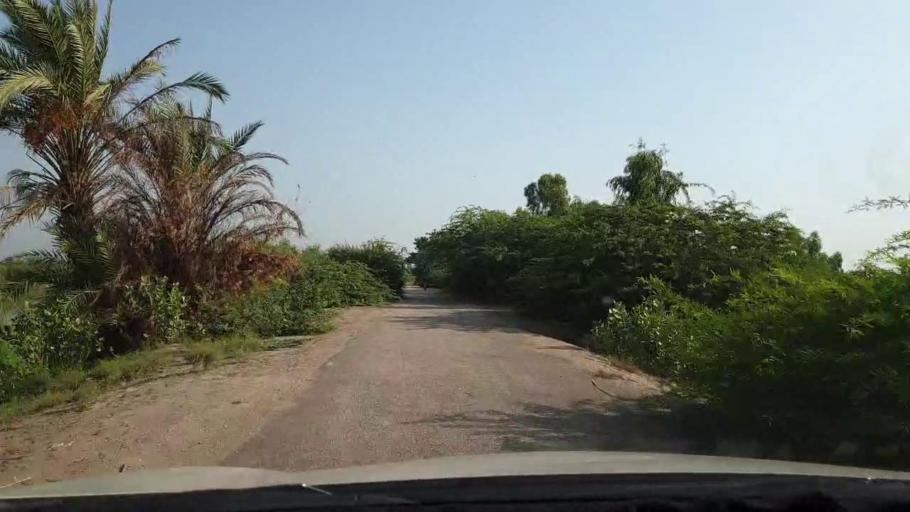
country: PK
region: Sindh
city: Larkana
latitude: 27.5552
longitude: 68.2567
